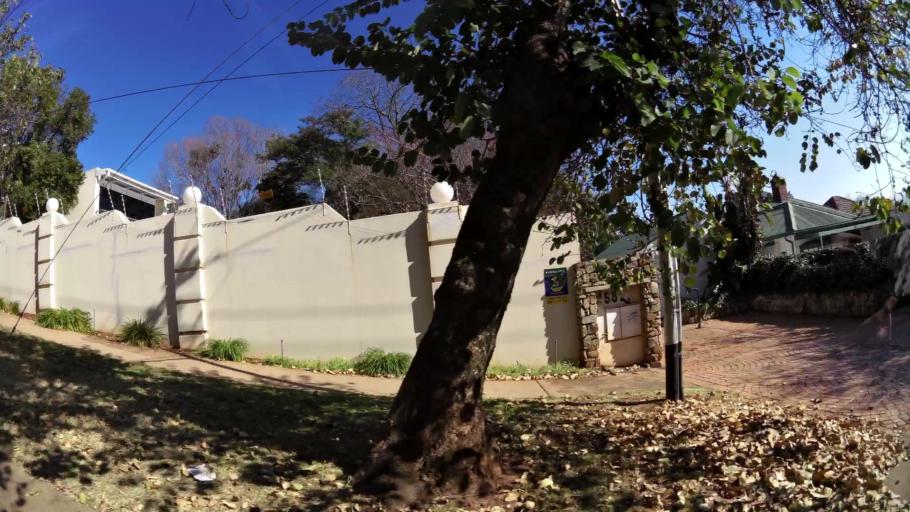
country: ZA
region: Gauteng
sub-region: City of Tshwane Metropolitan Municipality
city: Pretoria
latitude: -25.7615
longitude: 28.2047
